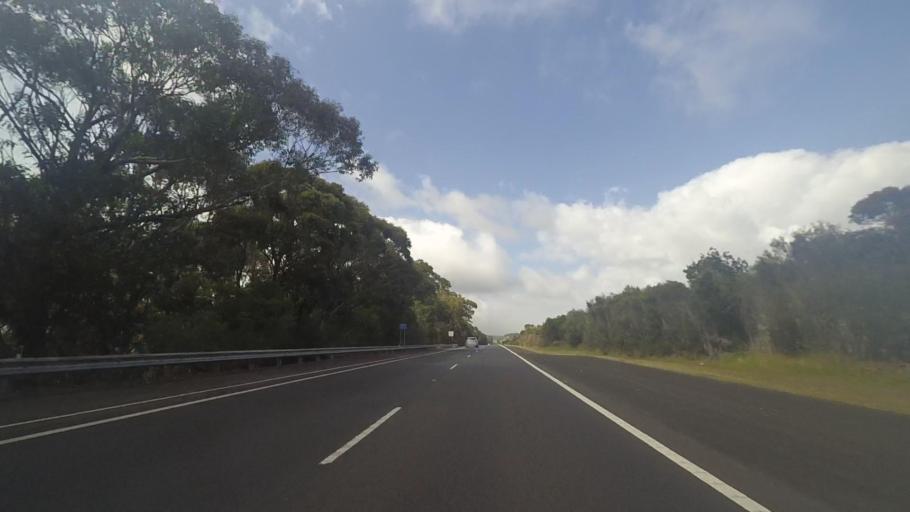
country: AU
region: New South Wales
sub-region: Wollongong
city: Helensburgh
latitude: -34.2094
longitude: 150.9619
